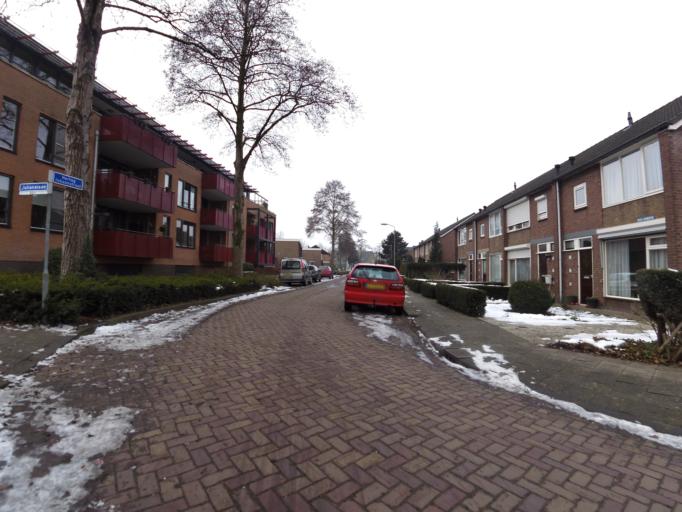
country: NL
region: Gelderland
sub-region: Gemeente Zevenaar
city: Zevenaar
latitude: 51.9311
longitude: 6.0720
